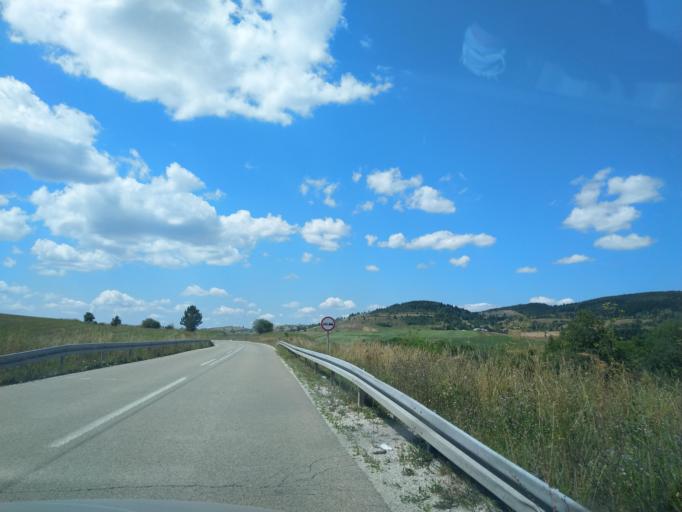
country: RS
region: Central Serbia
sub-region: Zlatiborski Okrug
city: Sjenica
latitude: 43.3299
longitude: 19.8761
